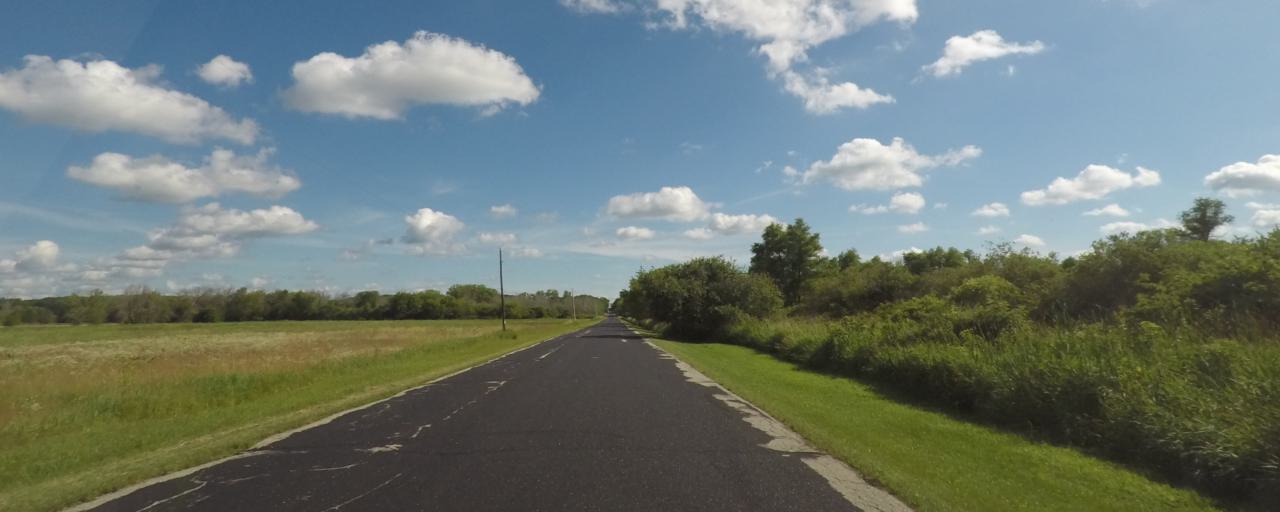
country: US
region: Wisconsin
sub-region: Rock County
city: Edgerton
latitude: 42.8791
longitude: -89.1321
